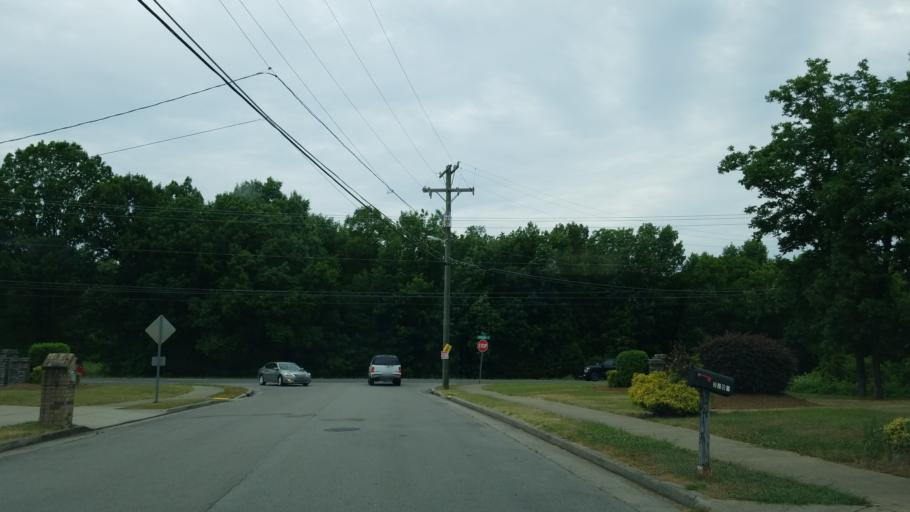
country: US
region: Tennessee
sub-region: Rutherford County
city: La Vergne
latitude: 36.0613
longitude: -86.5938
